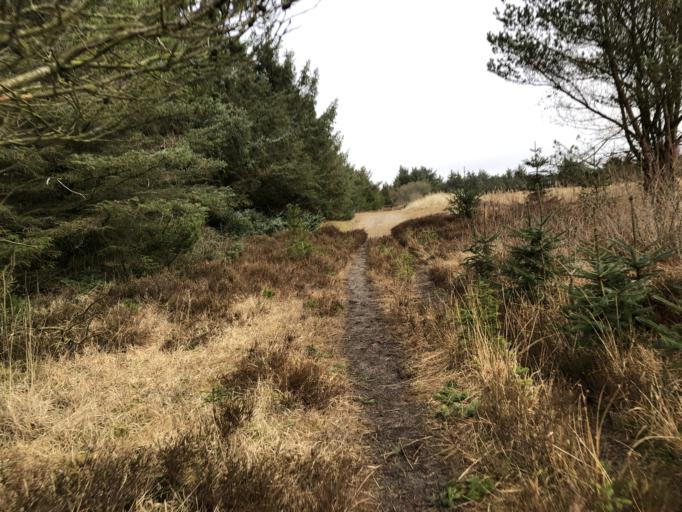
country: DK
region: Central Jutland
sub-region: Holstebro Kommune
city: Ulfborg
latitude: 56.3132
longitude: 8.1372
